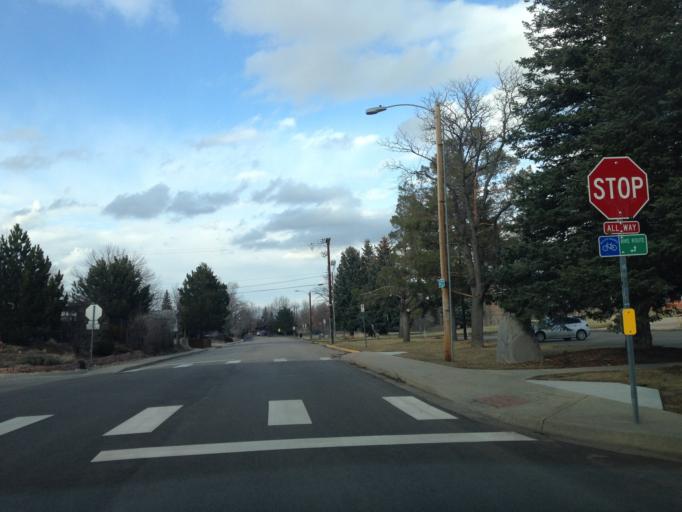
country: US
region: Colorado
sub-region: Boulder County
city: Boulder
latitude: 39.9746
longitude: -105.2499
